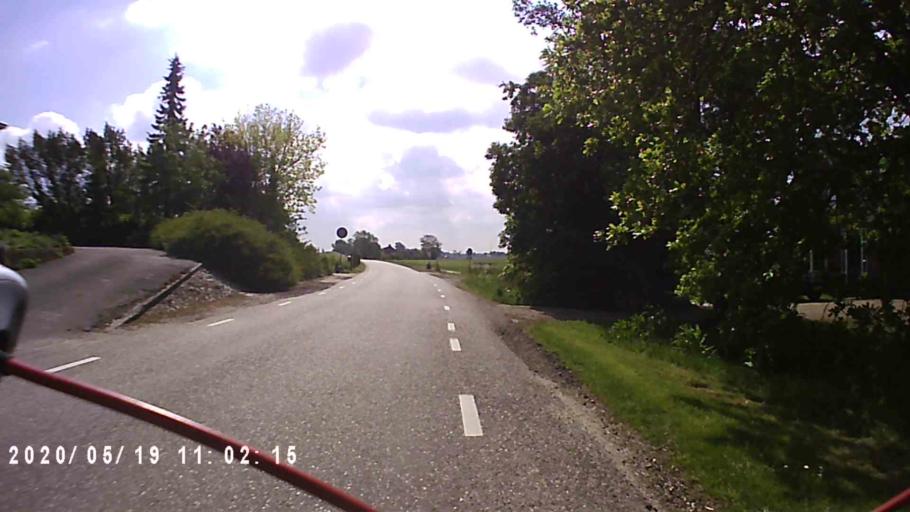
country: NL
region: Groningen
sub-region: Gemeente Zuidhorn
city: Grijpskerk
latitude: 53.3008
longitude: 6.2767
